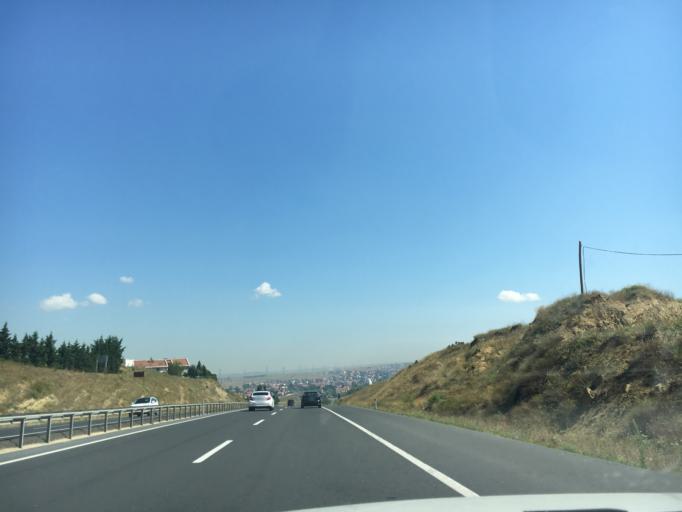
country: TR
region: Tekirdag
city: Sultankoy
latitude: 41.0008
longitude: 27.9758
